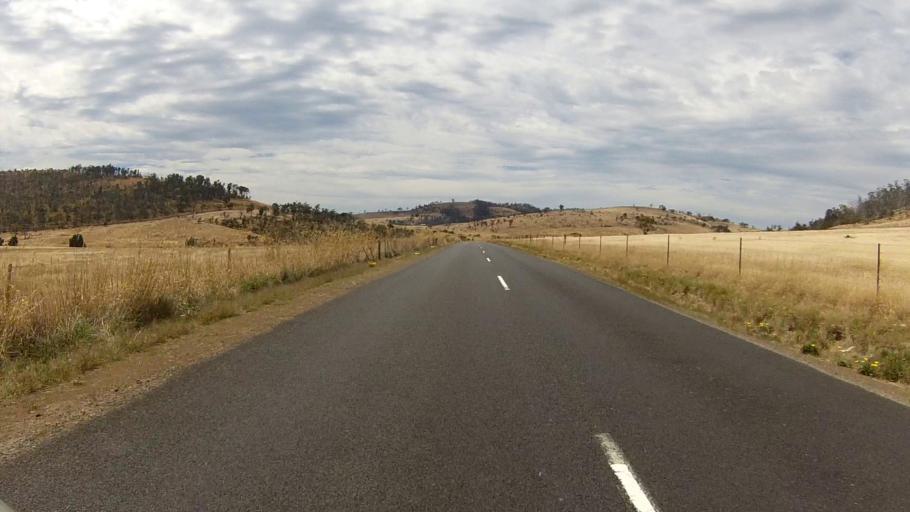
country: AU
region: Tasmania
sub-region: Sorell
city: Sorell
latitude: -42.8716
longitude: 147.6866
